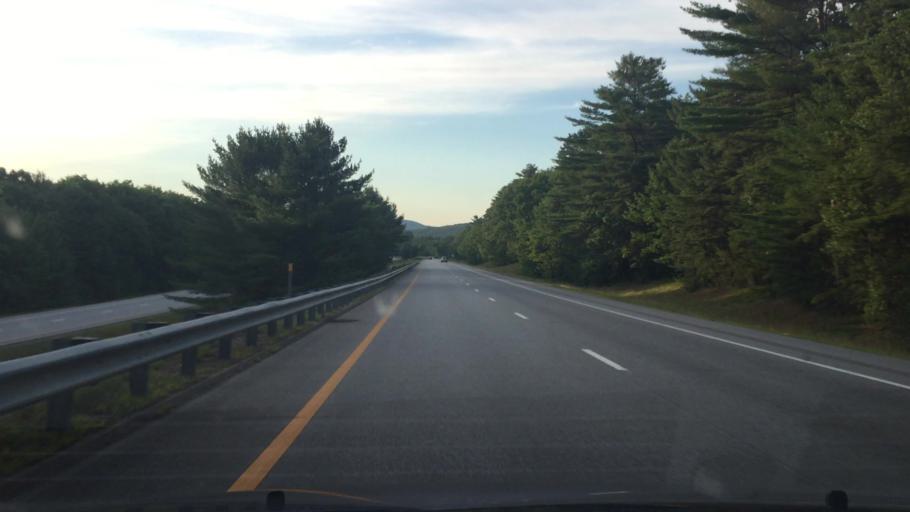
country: US
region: New Hampshire
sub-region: Grafton County
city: Plymouth
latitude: 43.7311
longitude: -71.6575
